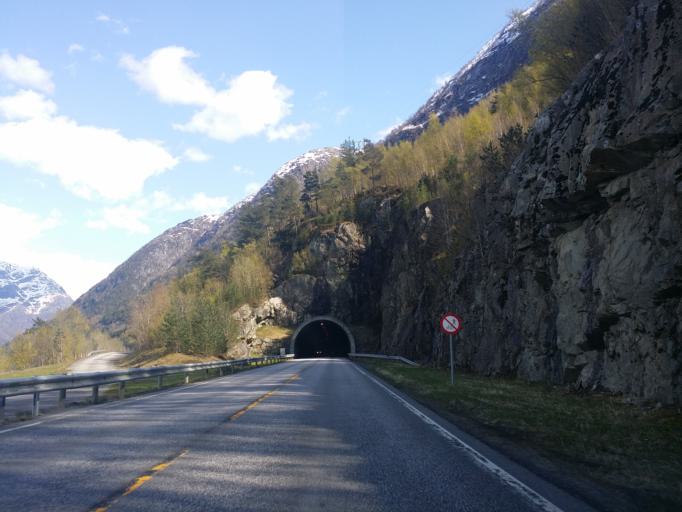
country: NO
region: Hordaland
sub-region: Ulvik
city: Ulvik
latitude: 60.4714
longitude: 6.9257
